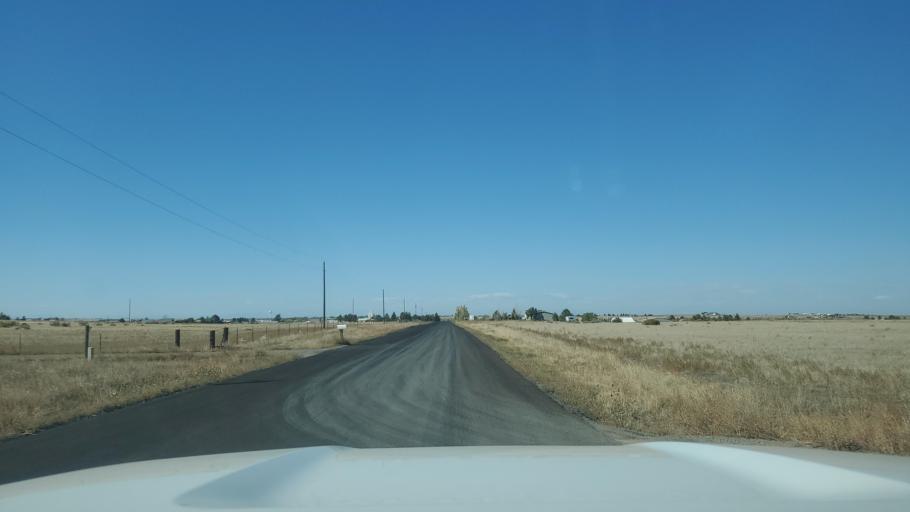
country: US
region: Colorado
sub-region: Adams County
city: Bennett
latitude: 39.7600
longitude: -104.3820
